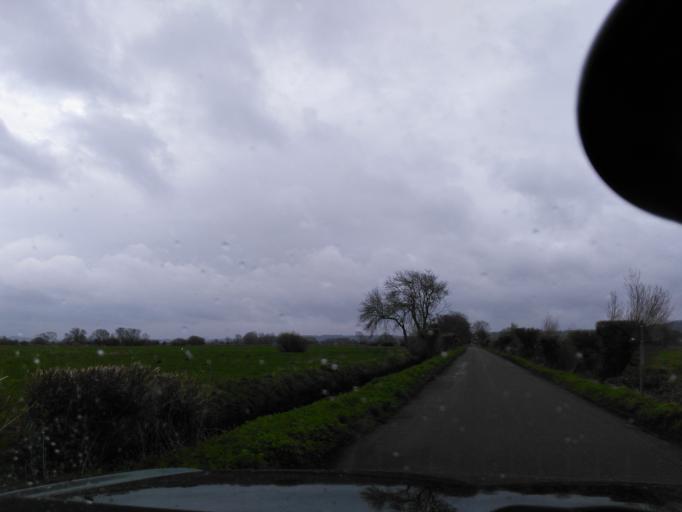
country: GB
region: England
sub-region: Somerset
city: Langport
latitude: 51.1074
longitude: -2.8194
